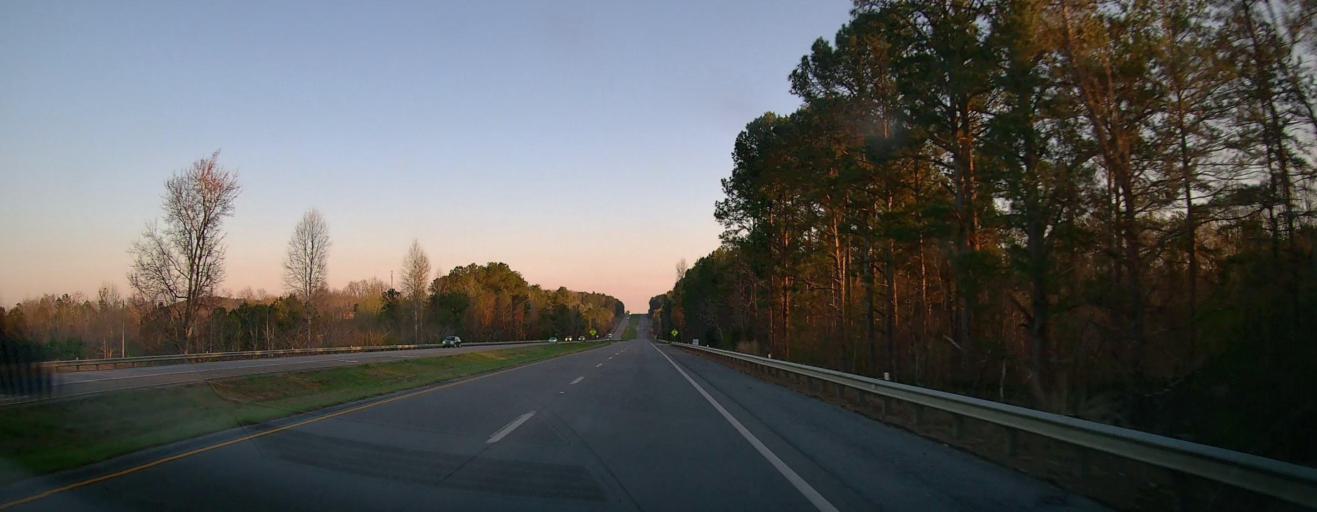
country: US
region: Alabama
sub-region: Talladega County
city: Sylacauga
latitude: 33.1368
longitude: -86.2488
